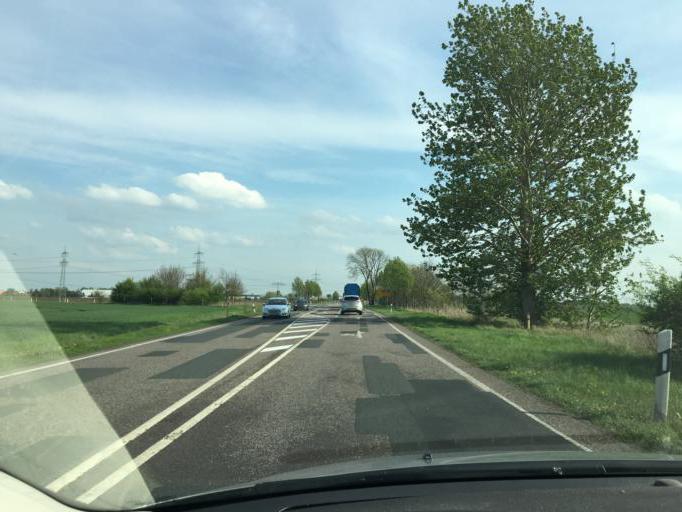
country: DE
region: Saxony-Anhalt
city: Meitzendorf
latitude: 52.2163
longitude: 11.5430
